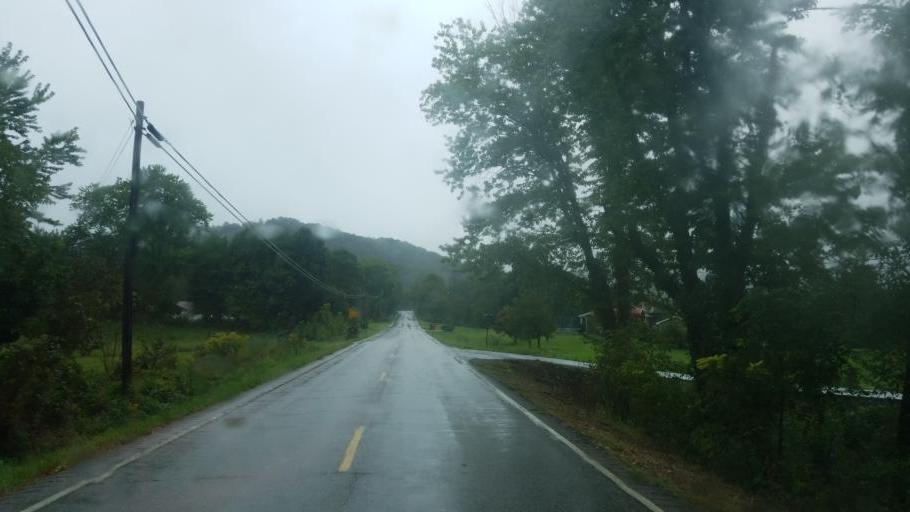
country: US
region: Kentucky
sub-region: Greenup County
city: South Shore
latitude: 38.6877
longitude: -82.9281
